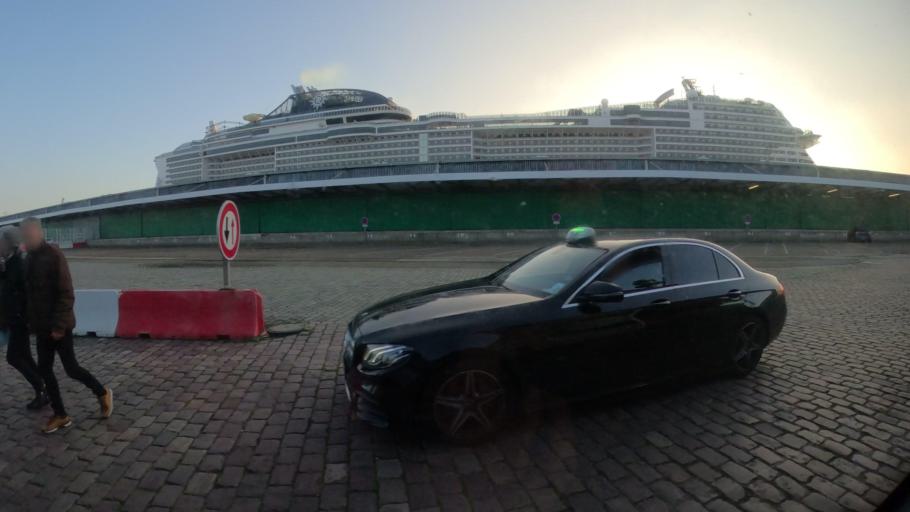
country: FR
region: Haute-Normandie
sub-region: Departement de la Seine-Maritime
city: Le Havre
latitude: 49.4815
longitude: 0.1092
